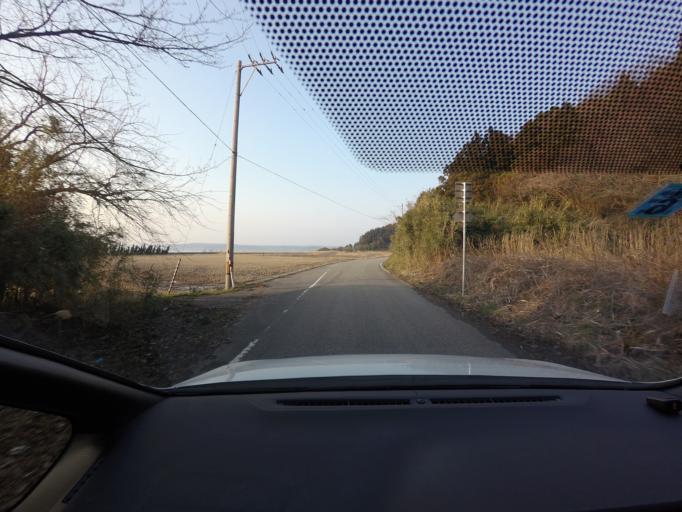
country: JP
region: Ishikawa
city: Nanao
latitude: 37.1523
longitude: 137.0255
